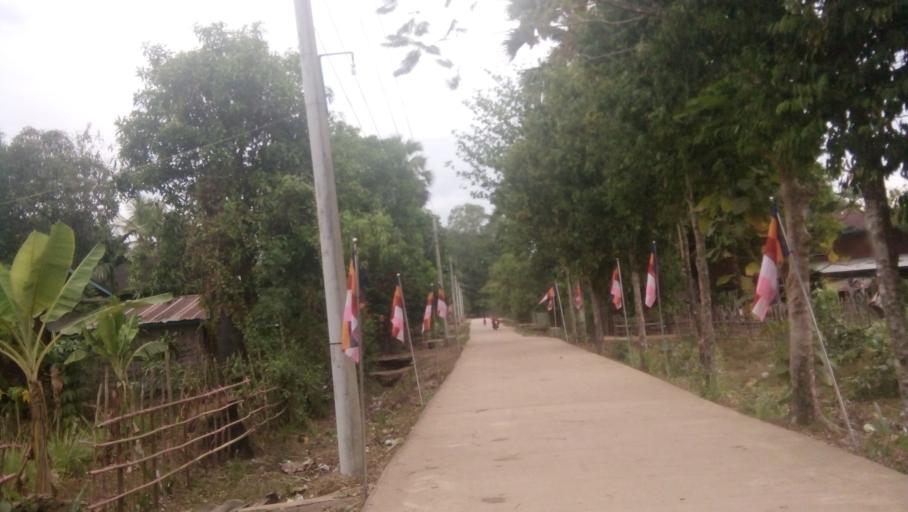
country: MM
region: Kayin
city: Hpa-an
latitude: 17.1164
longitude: 97.8174
